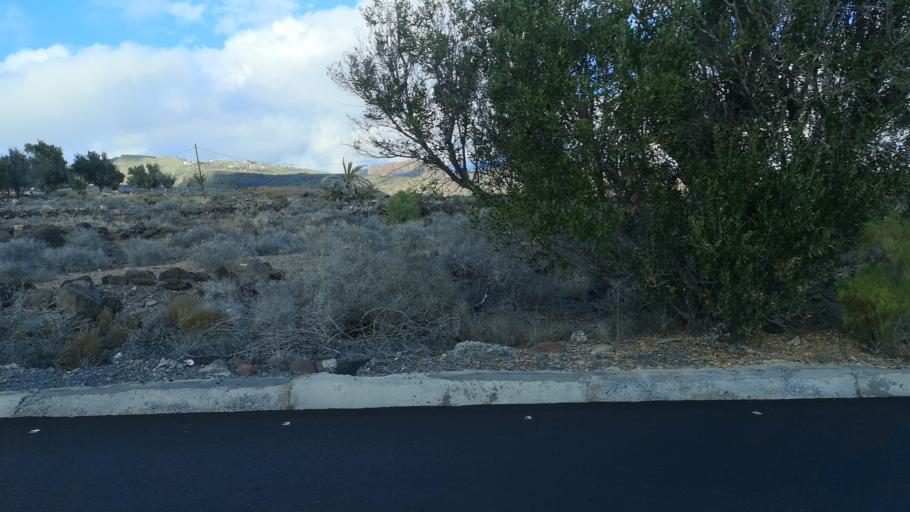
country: ES
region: Canary Islands
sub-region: Provincia de Santa Cruz de Tenerife
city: Alajero
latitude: 28.0503
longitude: -17.1994
